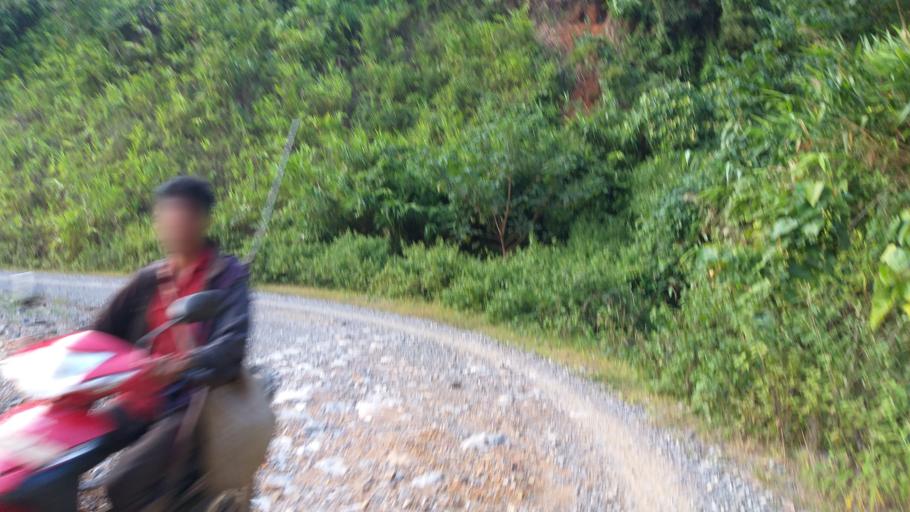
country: LA
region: Phongsali
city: Khoa
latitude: 21.1922
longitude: 102.5606
